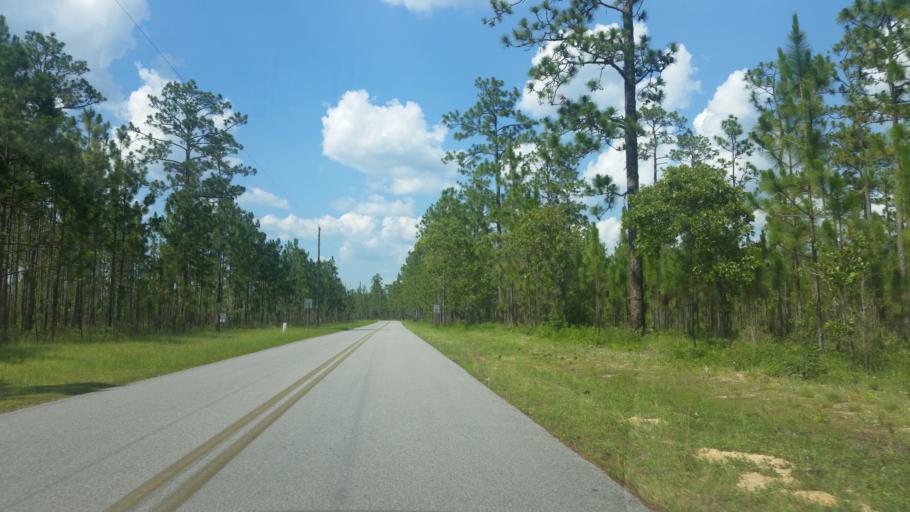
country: US
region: Florida
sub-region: Santa Rosa County
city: East Milton
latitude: 30.6922
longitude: -86.8757
